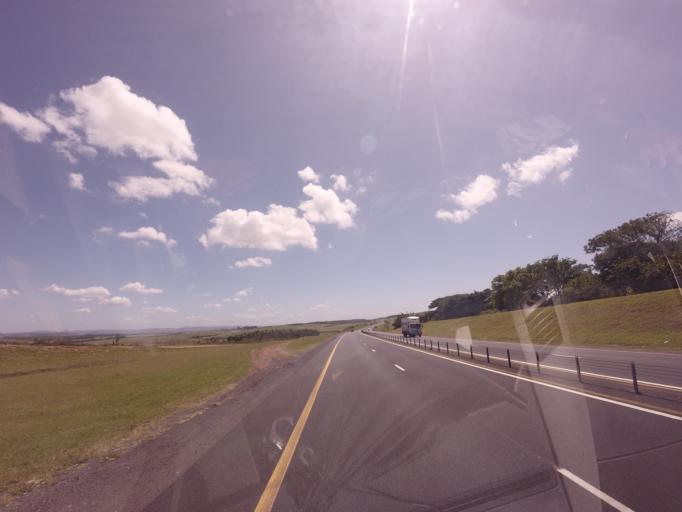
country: ZA
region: KwaZulu-Natal
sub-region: iLembe District Municipality
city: Mandeni
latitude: -29.0571
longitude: 31.6298
